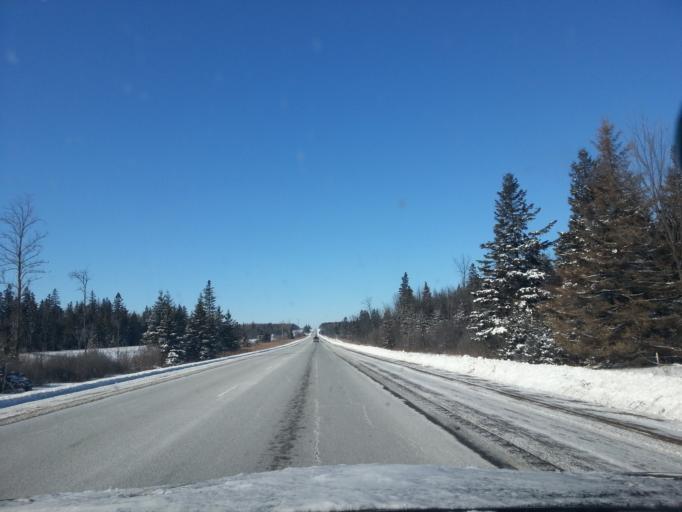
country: CA
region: Ontario
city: Carleton Place
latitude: 45.3233
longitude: -76.1106
